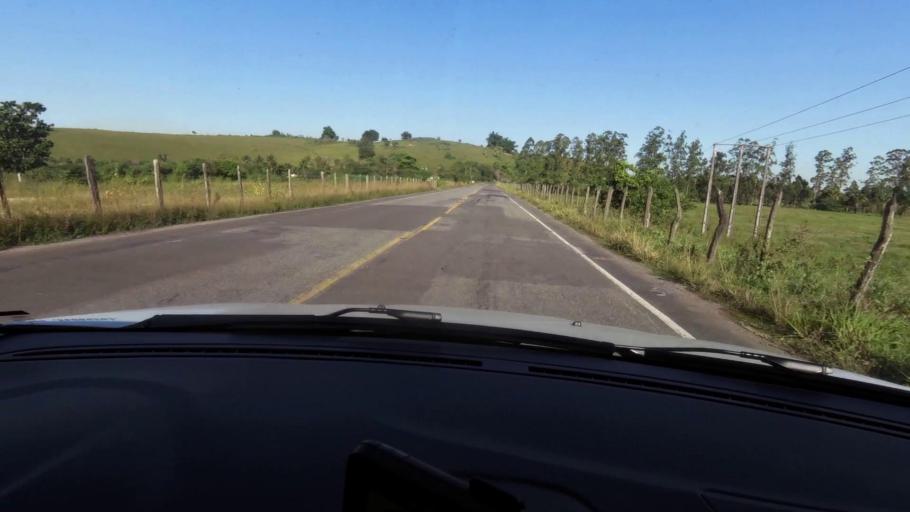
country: BR
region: Espirito Santo
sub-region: Alfredo Chaves
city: Alfredo Chaves
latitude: -20.7254
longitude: -40.6562
